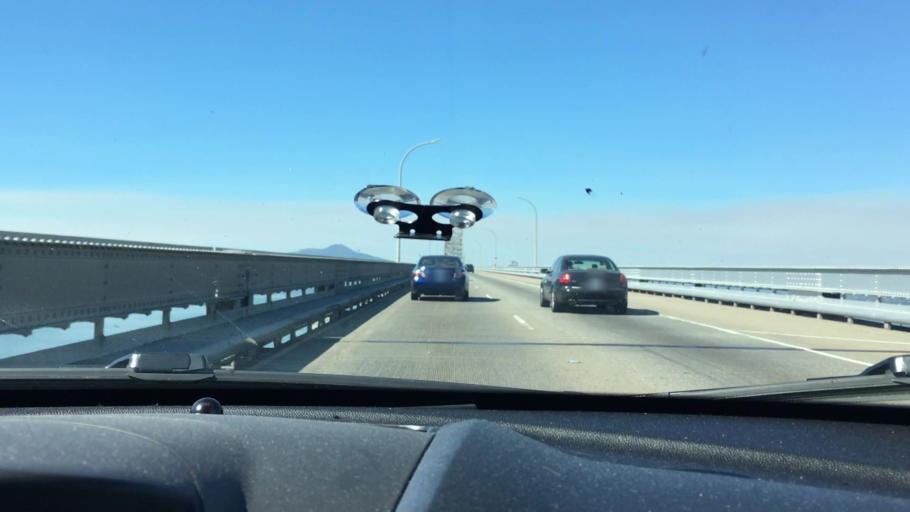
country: US
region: California
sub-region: Contra Costa County
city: North Richmond
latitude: 37.9333
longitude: -122.4172
